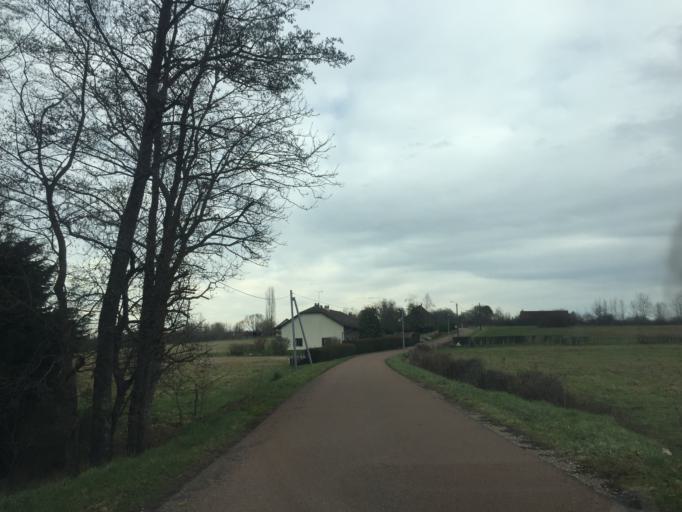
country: FR
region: Franche-Comte
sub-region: Departement du Jura
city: Mont-sous-Vaudrey
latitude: 46.8680
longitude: 5.5358
